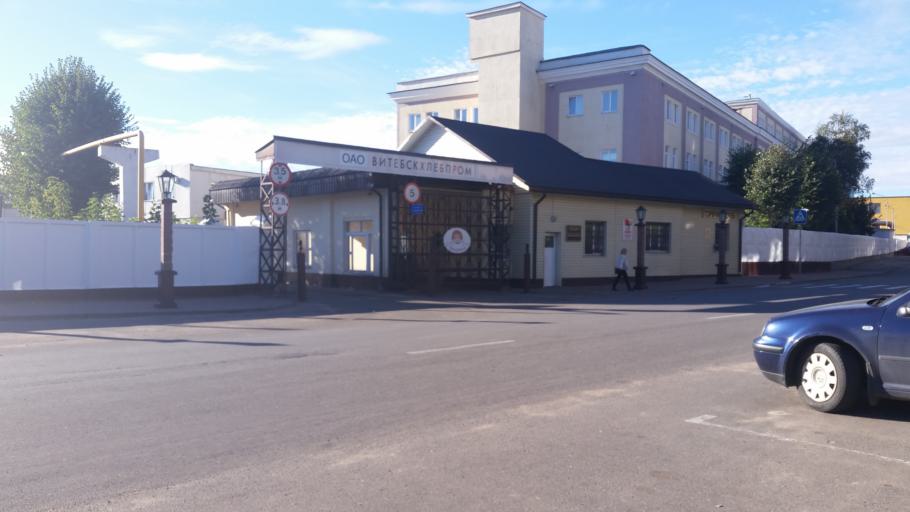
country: BY
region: Vitebsk
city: Vitebsk
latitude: 55.1800
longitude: 30.1875
